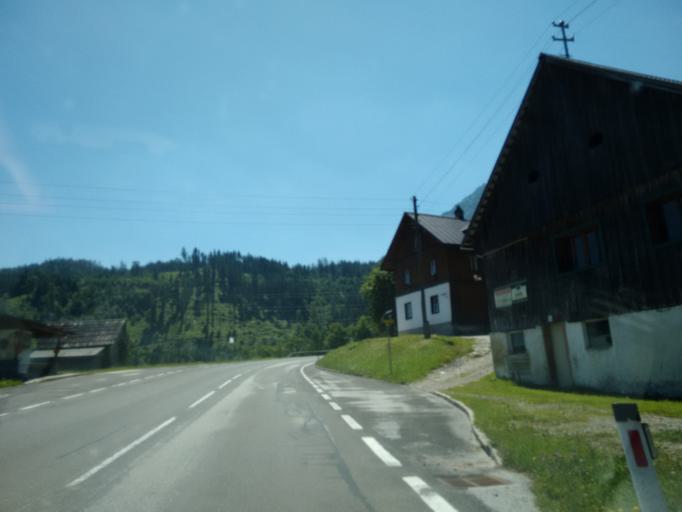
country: AT
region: Styria
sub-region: Politischer Bezirk Liezen
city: Altaussee
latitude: 47.6284
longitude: 13.7220
